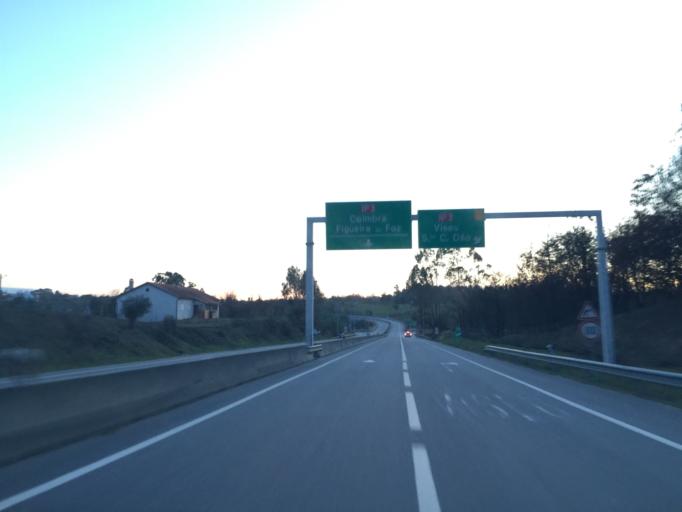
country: PT
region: Viseu
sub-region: Santa Comba Dao
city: Santa Comba Dao
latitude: 40.3857
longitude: -8.1145
